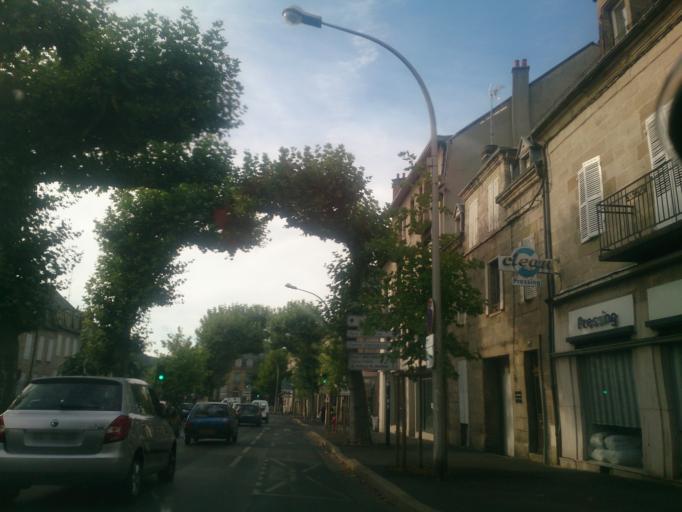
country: FR
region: Limousin
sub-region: Departement de la Correze
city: Brive-la-Gaillarde
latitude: 45.1596
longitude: 1.5357
